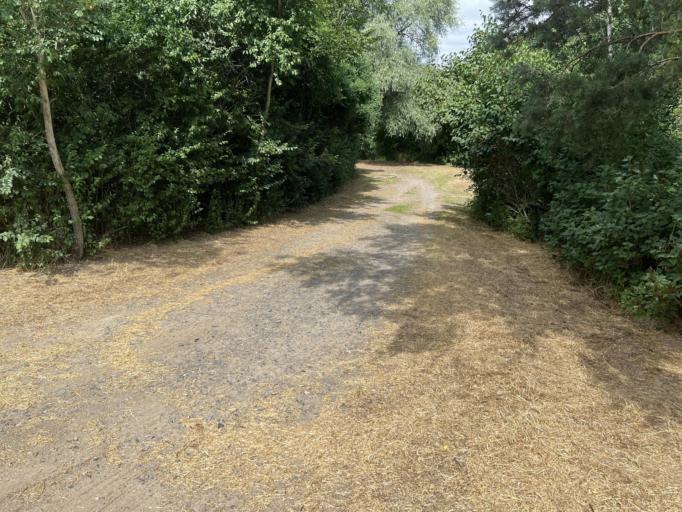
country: DE
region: Brandenburg
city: Wildau
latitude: 52.3293
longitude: 13.6175
